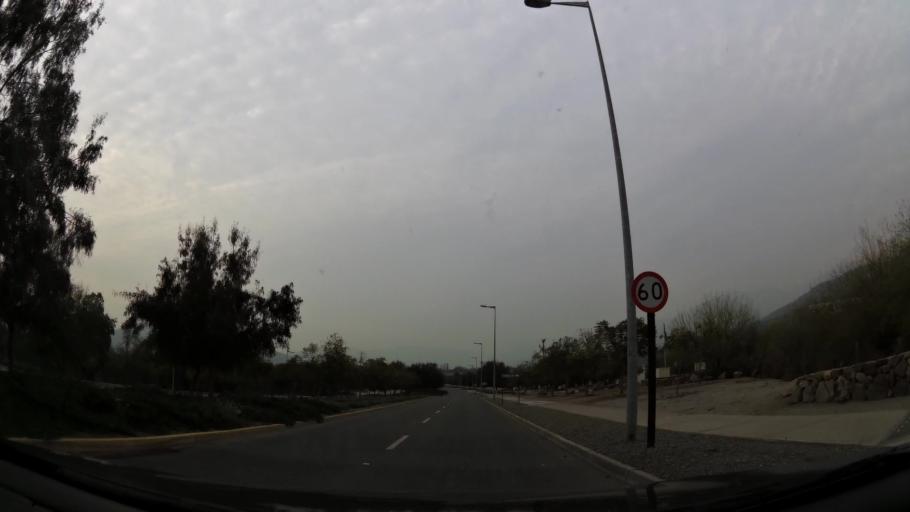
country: CL
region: Santiago Metropolitan
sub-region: Provincia de Chacabuco
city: Chicureo Abajo
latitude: -33.2710
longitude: -70.6243
